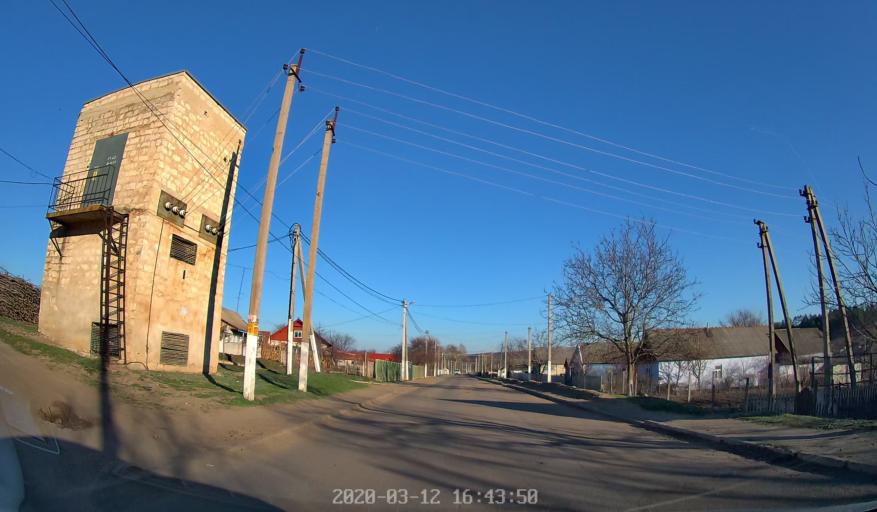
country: MD
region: Anenii Noi
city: Anenii Noi
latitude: 46.8187
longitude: 29.1457
